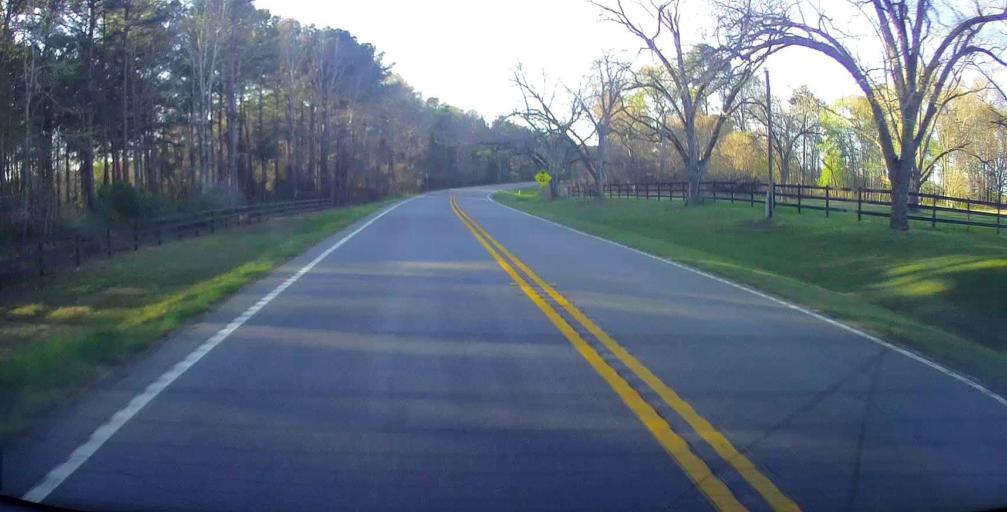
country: US
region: Georgia
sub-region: Pulaski County
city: Hawkinsville
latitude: 32.1665
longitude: -83.3597
